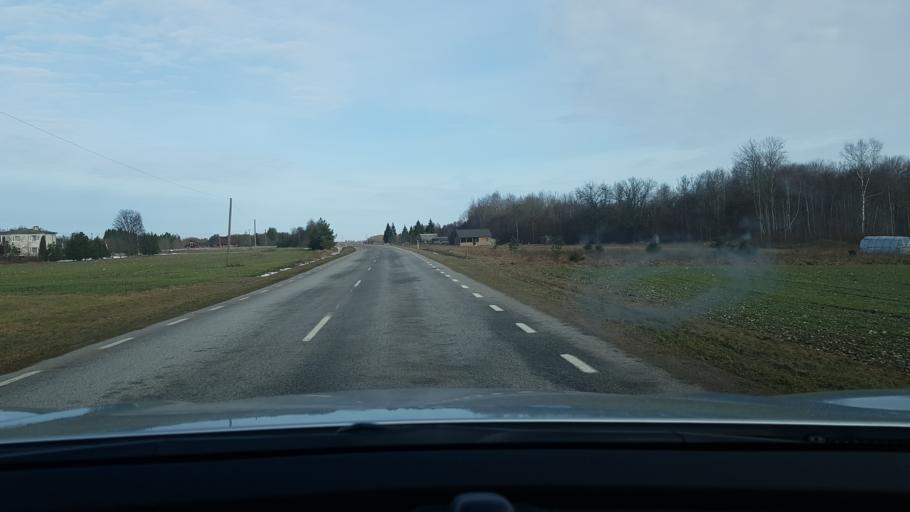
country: EE
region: Saare
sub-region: Kuressaare linn
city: Kuressaare
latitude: 58.5036
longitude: 22.7056
